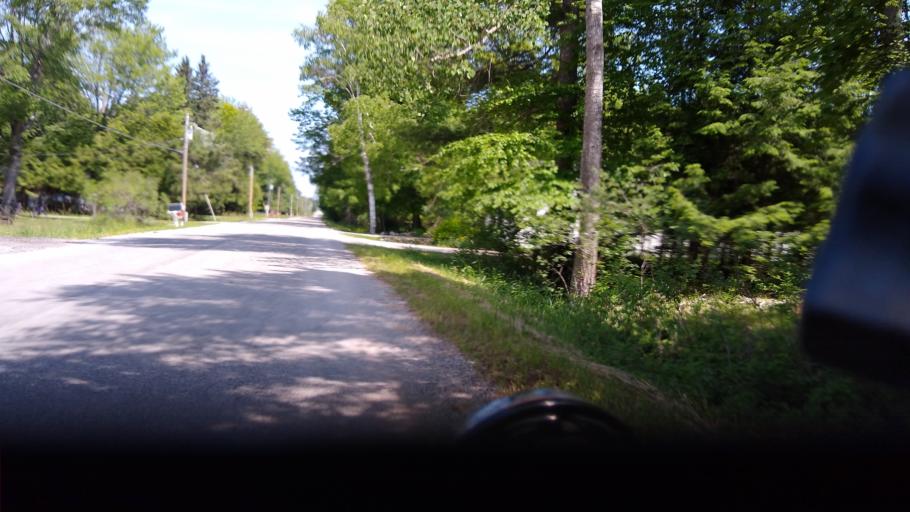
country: US
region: Michigan
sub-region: Delta County
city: Escanaba
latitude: 45.7100
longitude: -87.1435
